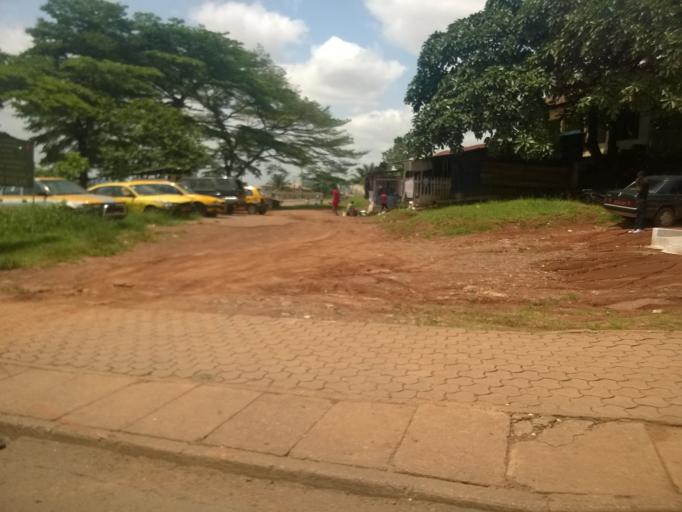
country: CM
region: Centre
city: Yaounde
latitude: 3.8597
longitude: 11.5051
